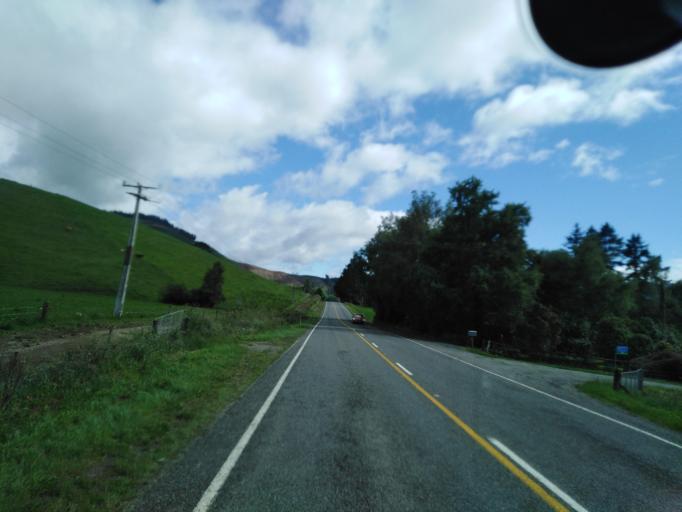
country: NZ
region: Nelson
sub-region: Nelson City
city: Nelson
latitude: -41.2759
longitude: 173.5731
